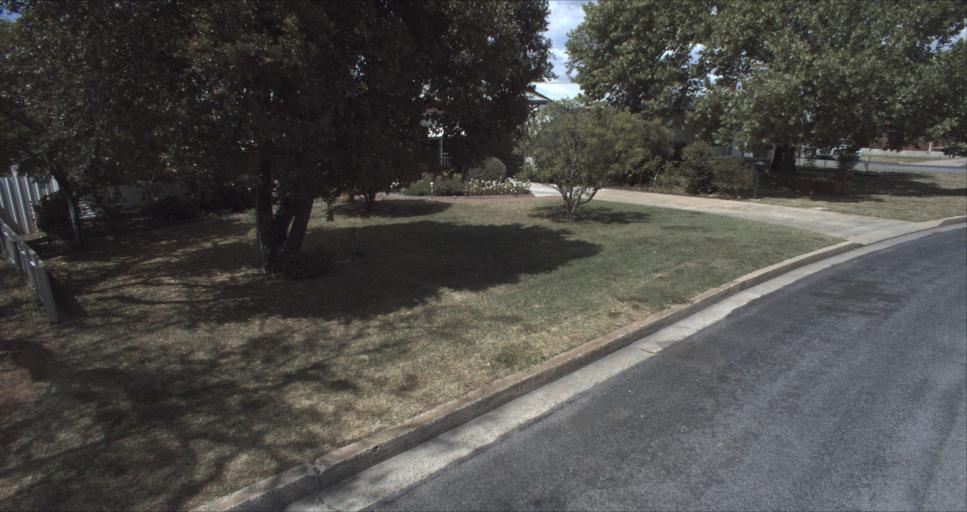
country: AU
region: New South Wales
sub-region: Leeton
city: Leeton
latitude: -34.5633
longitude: 146.3958
